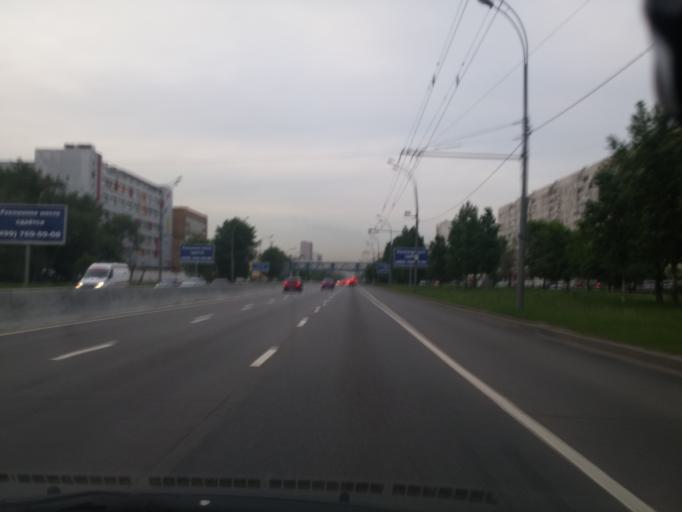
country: RU
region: Moscow
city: Altuf'yevskiy
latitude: 55.8810
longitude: 37.5865
